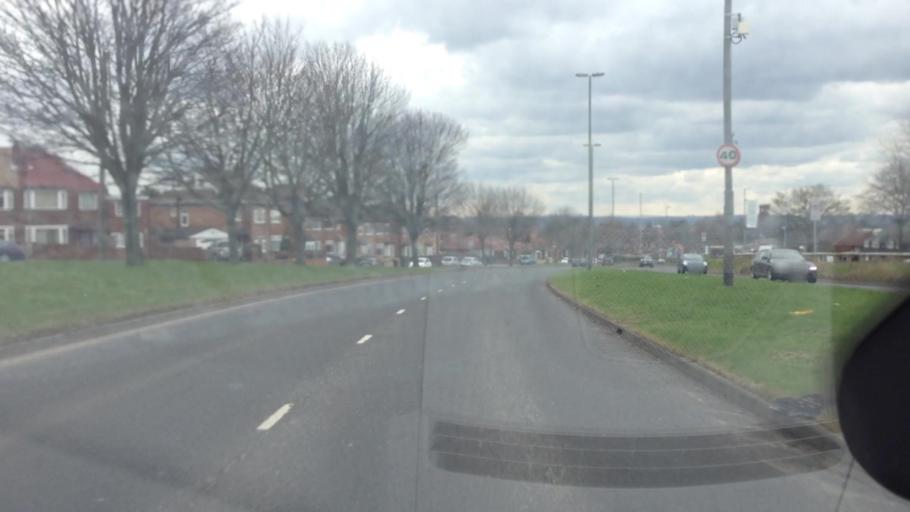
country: GB
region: England
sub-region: City and Borough of Leeds
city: Scholes
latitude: 53.8122
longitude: -1.4571
